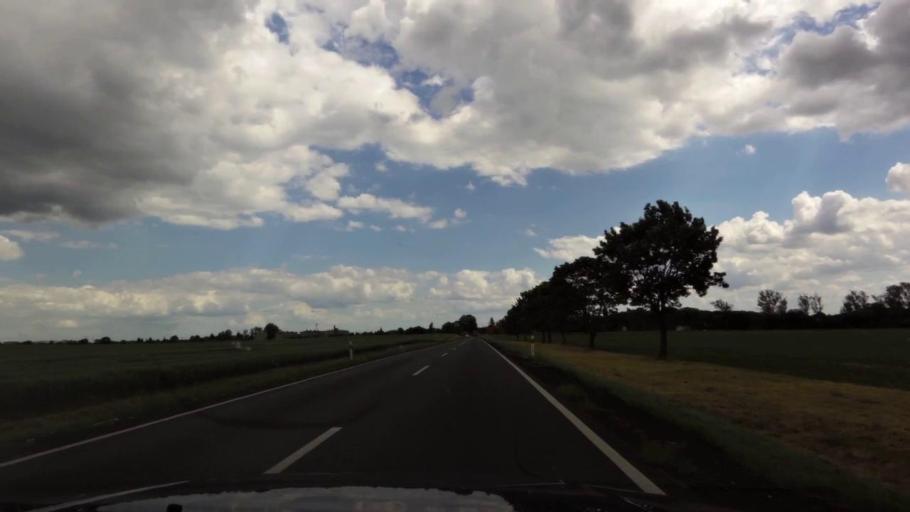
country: PL
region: West Pomeranian Voivodeship
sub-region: Powiat mysliborski
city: Mysliborz
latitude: 52.9531
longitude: 14.7780
